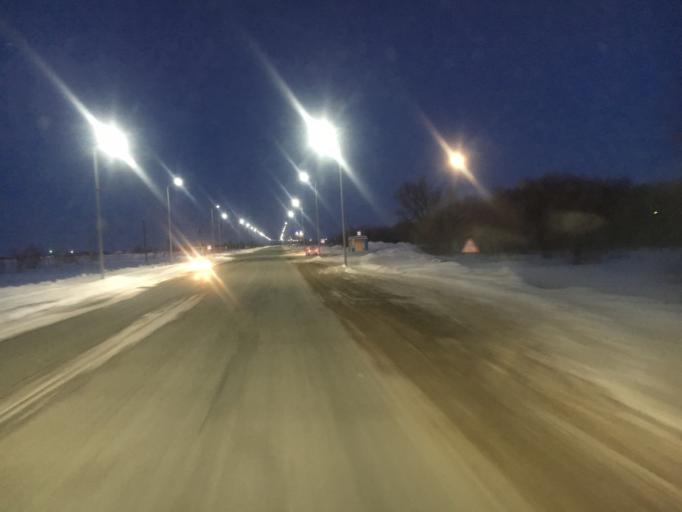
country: KZ
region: Batys Qazaqstan
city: Oral
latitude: 51.1578
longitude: 51.4999
